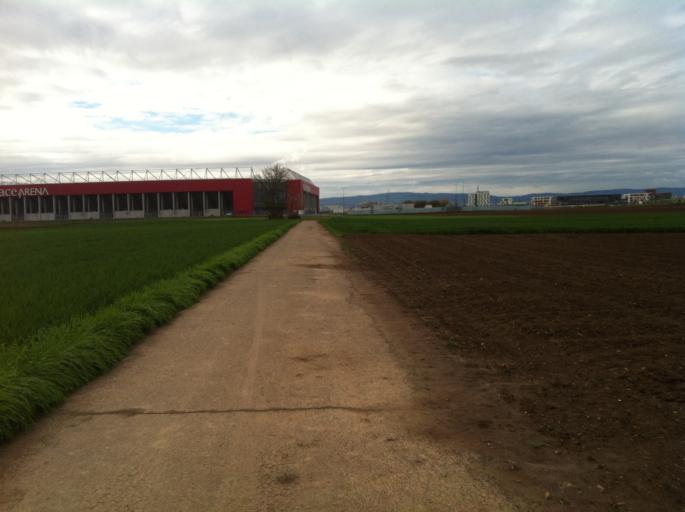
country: DE
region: Rheinland-Pfalz
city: Klein-Winternheim
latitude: 49.9812
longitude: 8.2288
